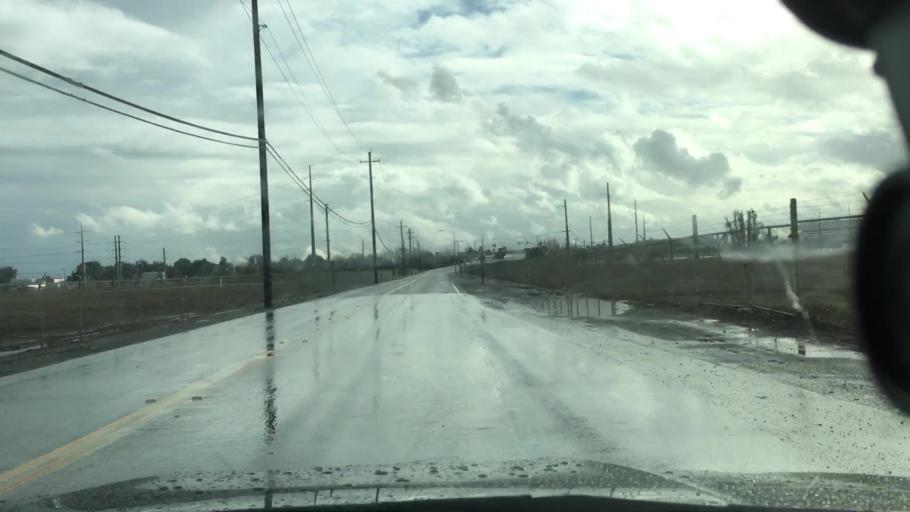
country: US
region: California
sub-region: Santa Clara County
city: Milpitas
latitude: 37.4256
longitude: -121.9403
